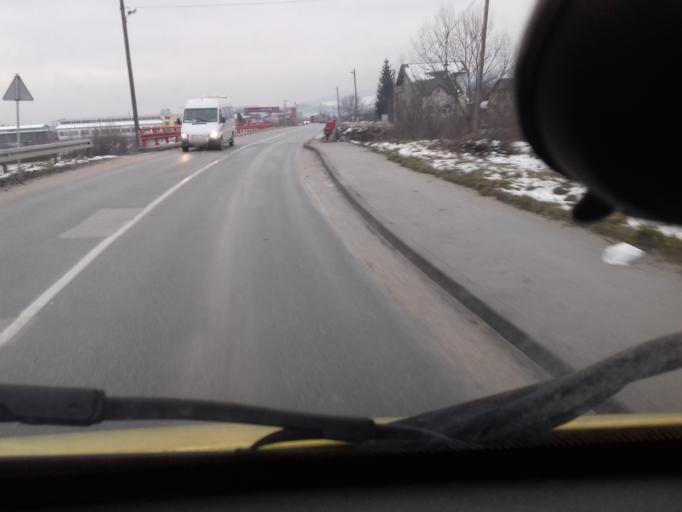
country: BA
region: Federation of Bosnia and Herzegovina
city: Vitez
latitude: 44.1676
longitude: 17.7687
